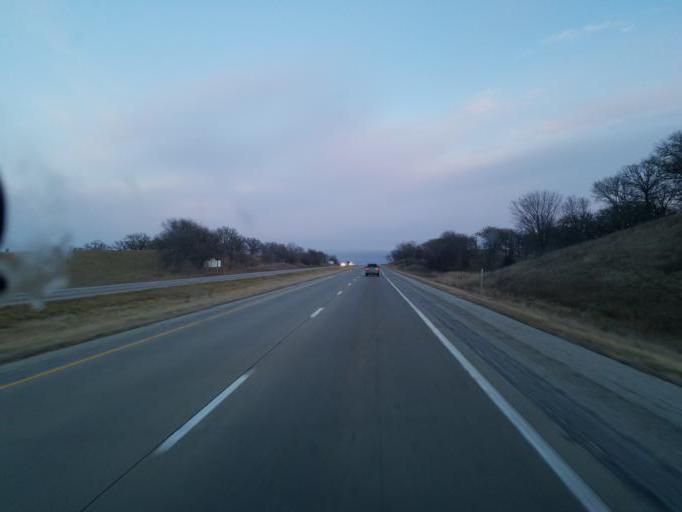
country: US
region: Iowa
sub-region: Pottawattamie County
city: Avoca
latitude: 41.4981
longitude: -95.3065
